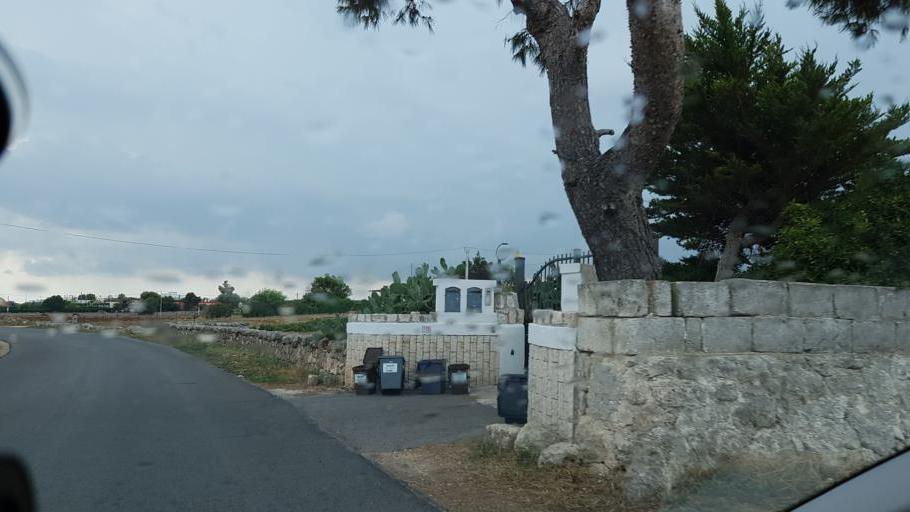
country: IT
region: Apulia
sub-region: Provincia di Bari
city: Monopoli
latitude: 40.9355
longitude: 17.3200
